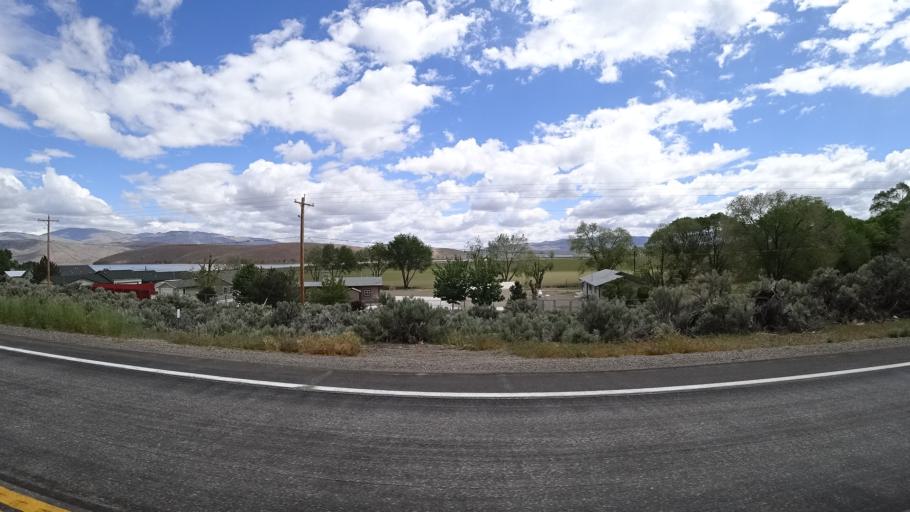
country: US
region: Nevada
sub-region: Lyon County
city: Smith Valley
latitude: 38.6515
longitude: -119.5347
